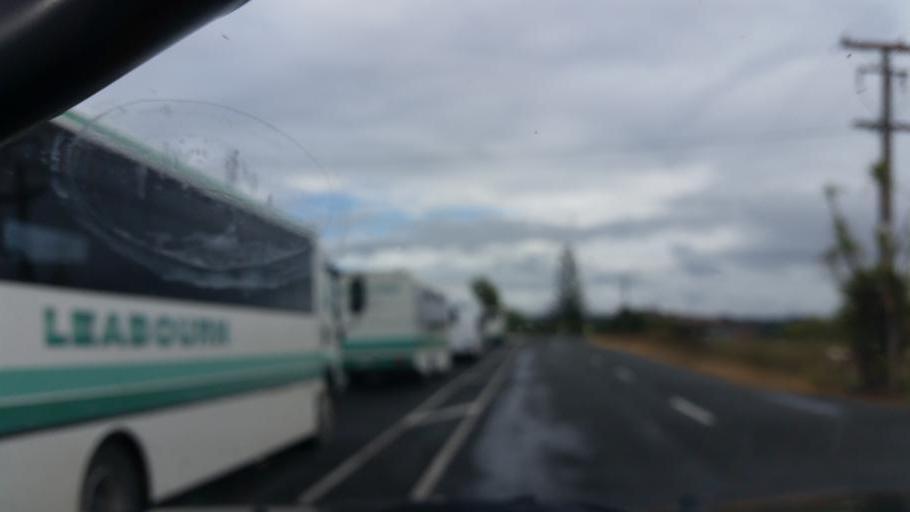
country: NZ
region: Northland
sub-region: Whangarei
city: Ruakaka
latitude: -36.1160
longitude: 174.3654
